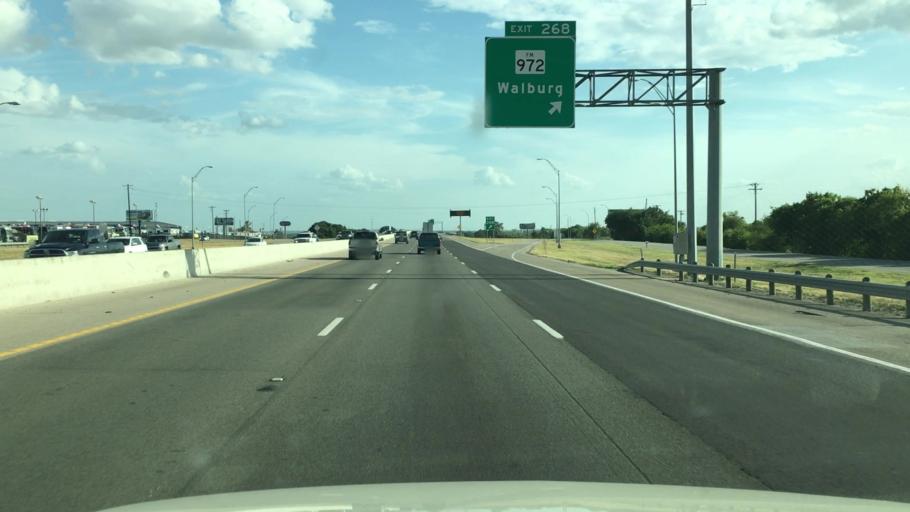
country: US
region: Texas
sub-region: Williamson County
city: Serenada
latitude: 30.7292
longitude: -97.6423
